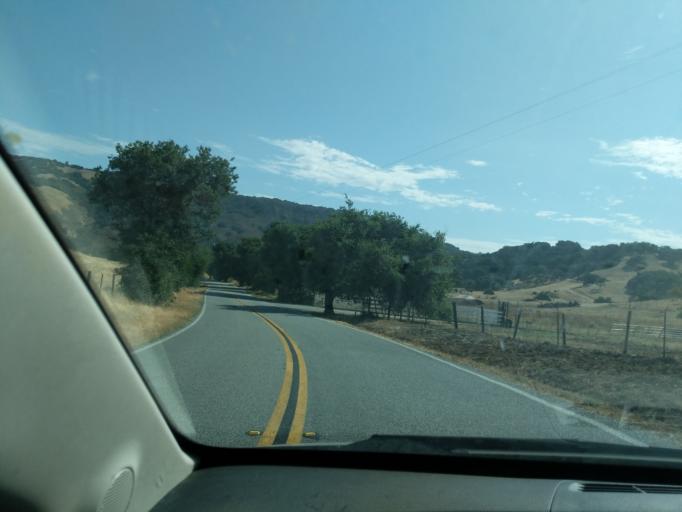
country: US
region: California
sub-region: Santa Clara County
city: Gilroy
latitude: 37.0680
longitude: -121.5215
